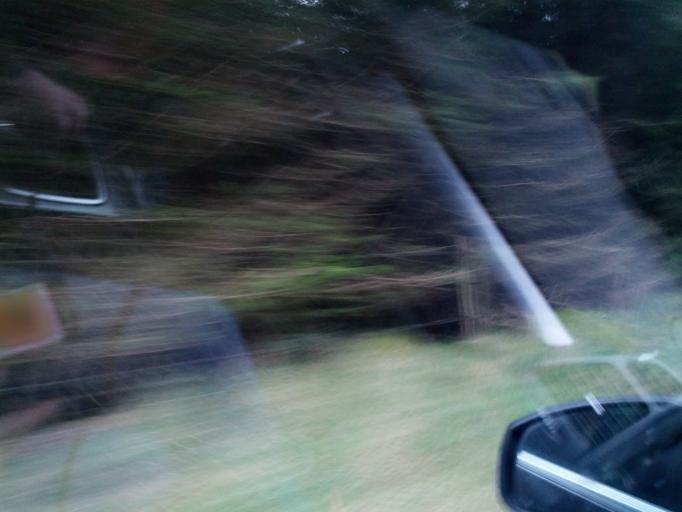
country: IE
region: Connaught
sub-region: County Galway
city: Athenry
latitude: 53.3810
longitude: -8.6370
